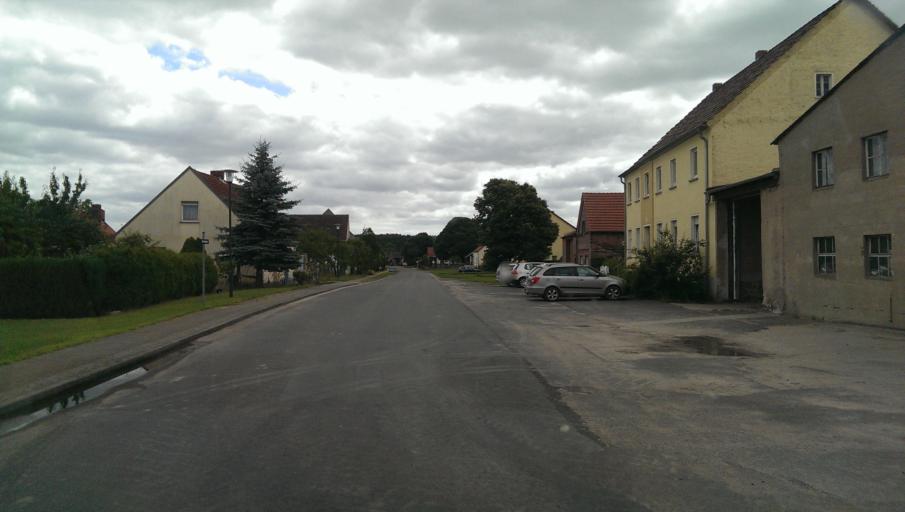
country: DE
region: Brandenburg
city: Belzig
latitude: 52.1009
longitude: 12.6177
